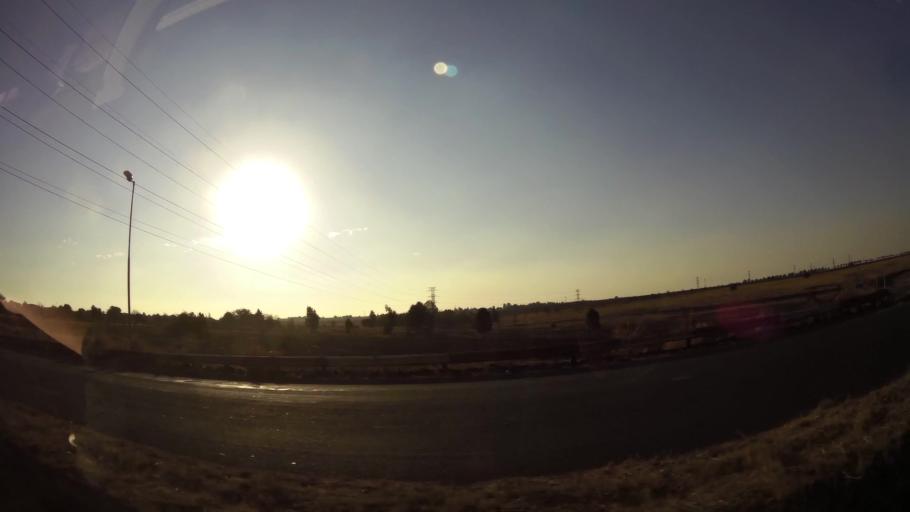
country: ZA
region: Gauteng
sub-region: West Rand District Municipality
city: Randfontein
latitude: -26.2055
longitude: 27.6623
